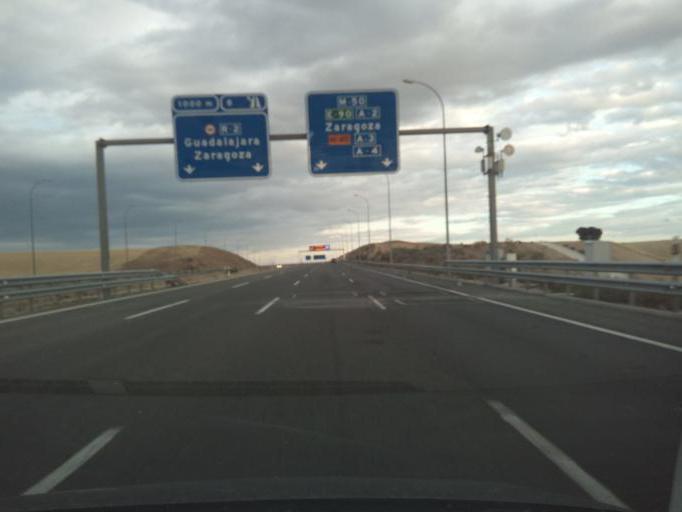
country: ES
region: Madrid
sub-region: Provincia de Madrid
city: Paracuellos de Jarama
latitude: 40.5303
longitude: -3.5190
